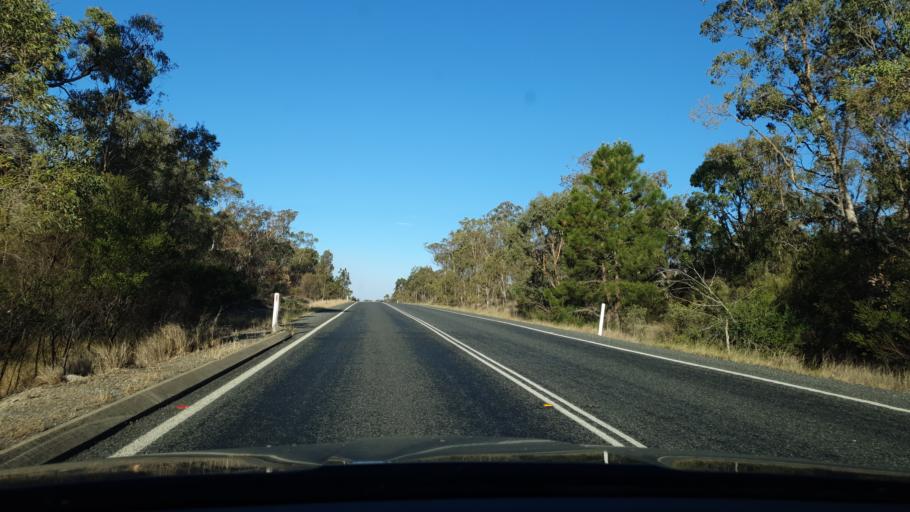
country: AU
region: Queensland
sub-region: Southern Downs
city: Stanthorpe
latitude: -28.6424
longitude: 151.9362
